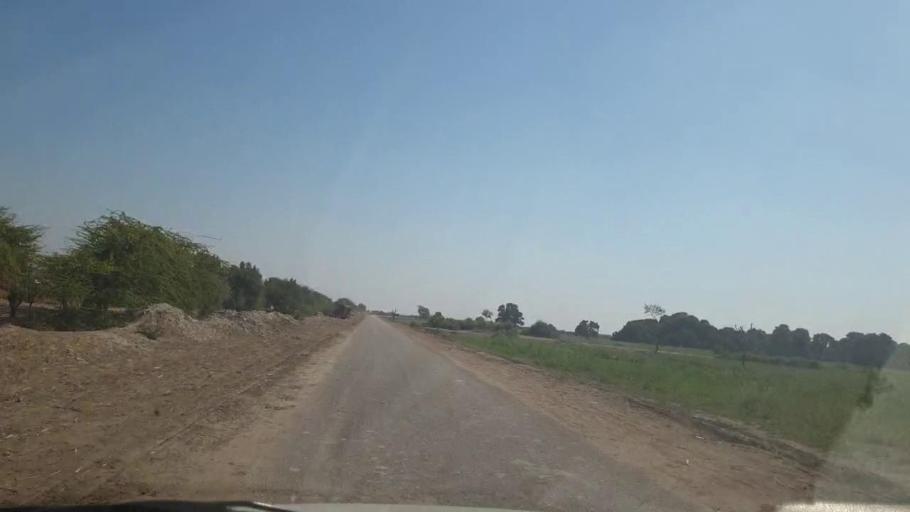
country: PK
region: Sindh
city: Mirpur Khas
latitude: 25.4635
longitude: 69.1798
